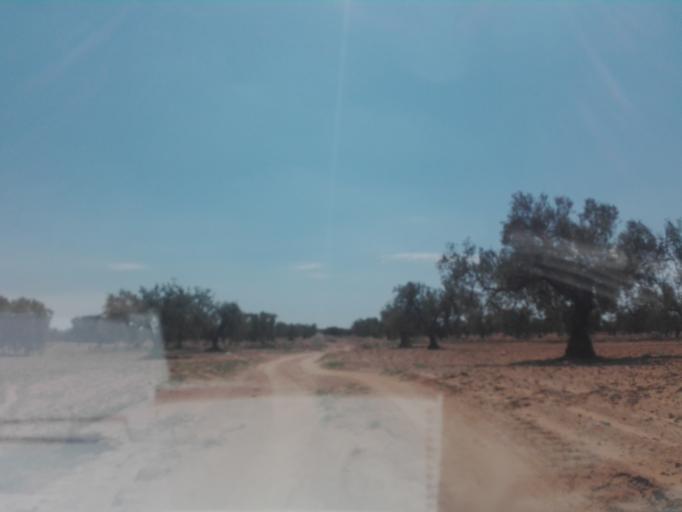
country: TN
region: Safaqis
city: Bi'r `Ali Bin Khalifah
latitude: 34.6098
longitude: 10.3536
